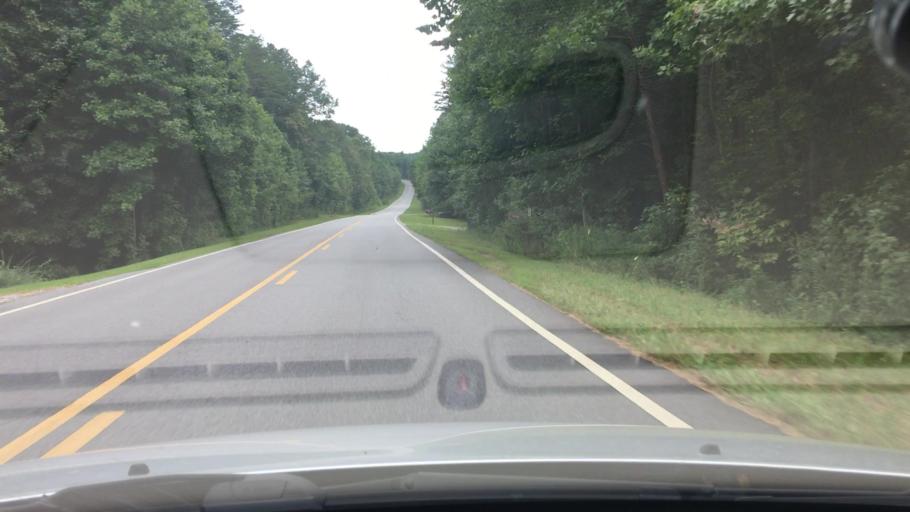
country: US
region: Georgia
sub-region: Lumpkin County
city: Dahlonega
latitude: 34.6165
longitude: -83.8992
